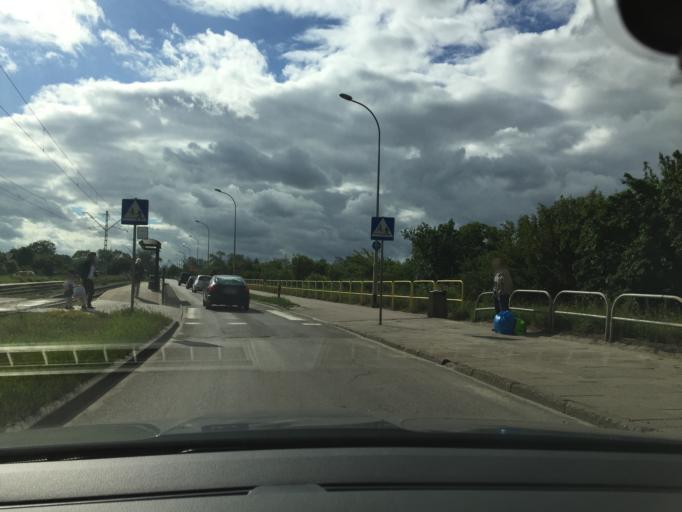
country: PL
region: Pomeranian Voivodeship
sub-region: Gdansk
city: Gdansk
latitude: 54.3628
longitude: 18.7049
